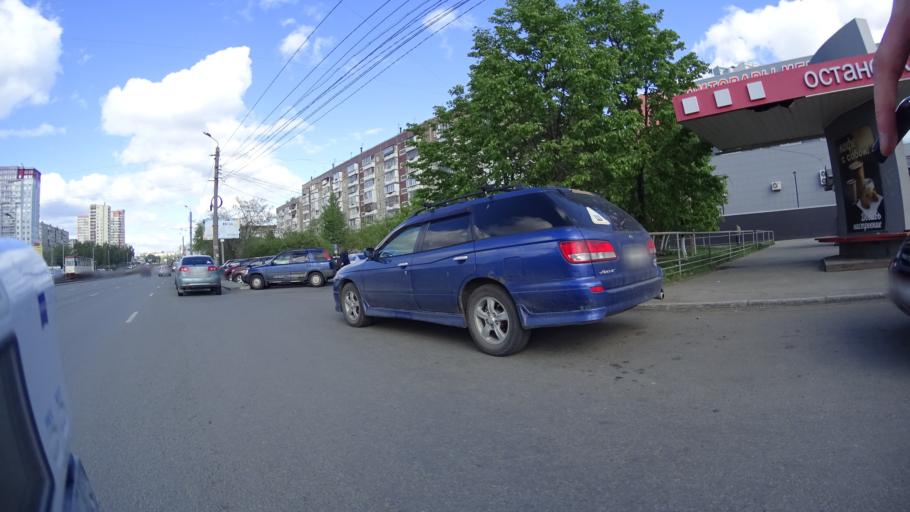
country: RU
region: Chelyabinsk
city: Roshchino
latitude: 55.1830
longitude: 61.2934
